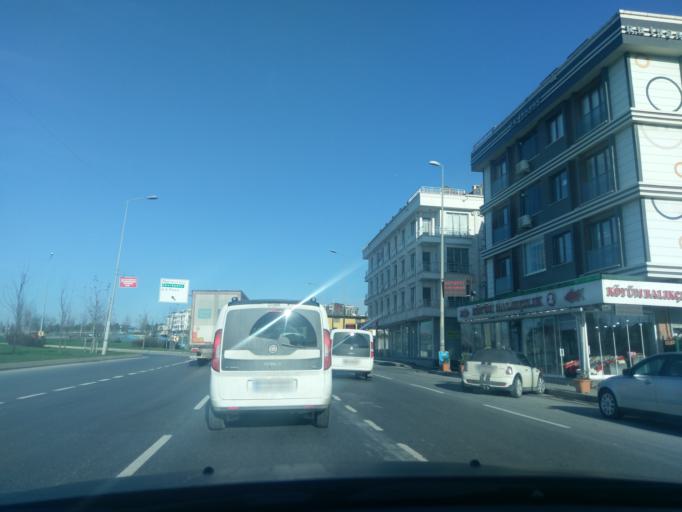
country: TR
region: Istanbul
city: Sultangazi
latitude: 41.1097
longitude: 28.8493
